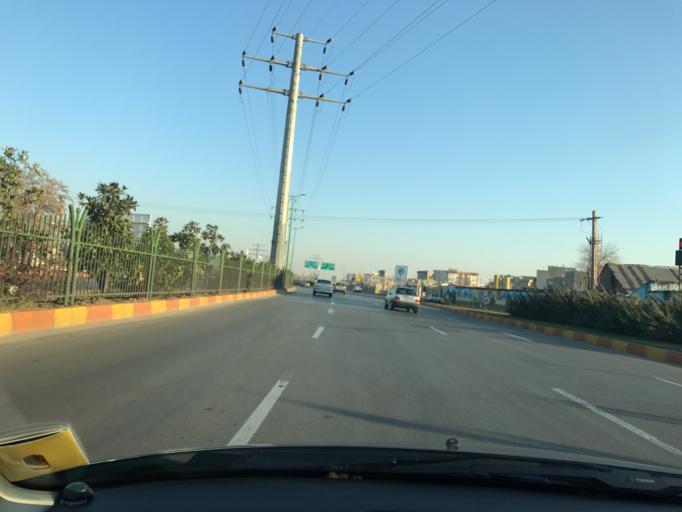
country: IR
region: Qazvin
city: Qazvin
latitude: 36.2869
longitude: 50.0114
